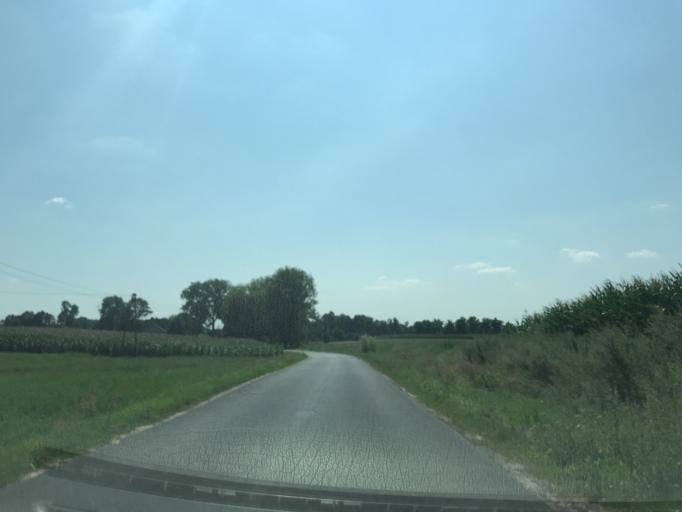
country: PL
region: Kujawsko-Pomorskie
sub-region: Powiat lipnowski
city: Kikol
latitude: 52.9180
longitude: 19.1731
